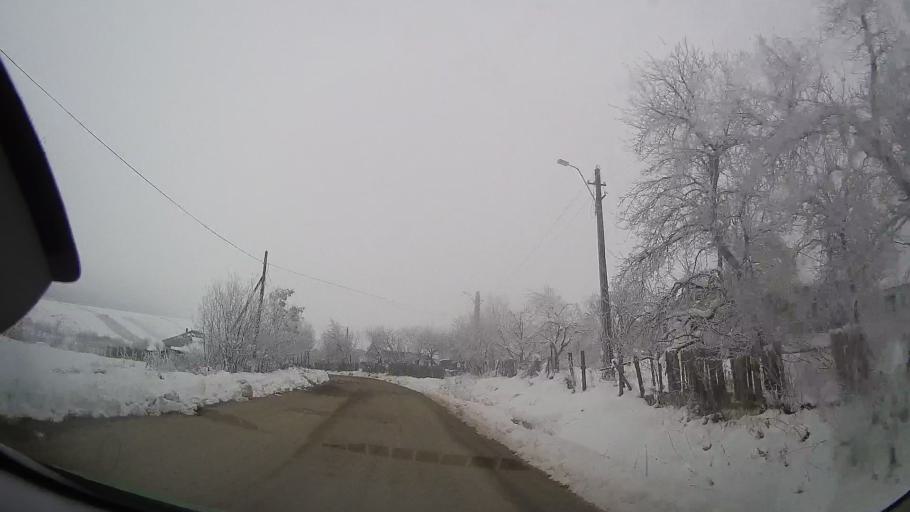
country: RO
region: Iasi
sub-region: Comuna Tansa
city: Tansa
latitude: 46.9140
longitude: 27.2253
